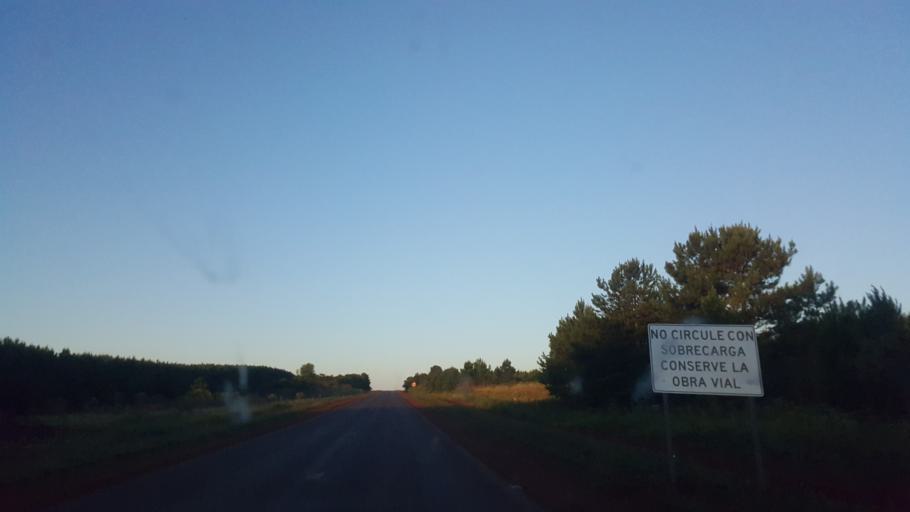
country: AR
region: Corrientes
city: Santo Tome
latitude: -28.4156
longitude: -55.9855
